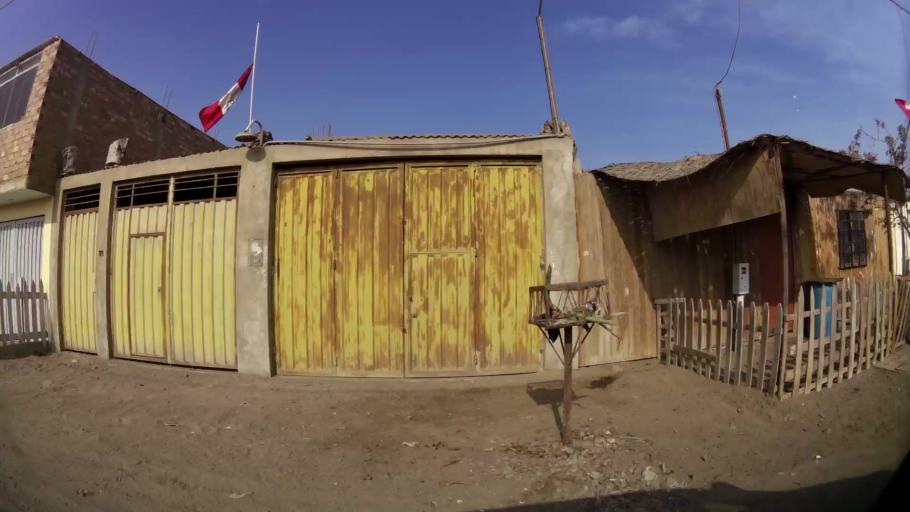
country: PE
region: Lima
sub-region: Lima
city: Santa Rosa
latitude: -11.7606
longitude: -77.1685
